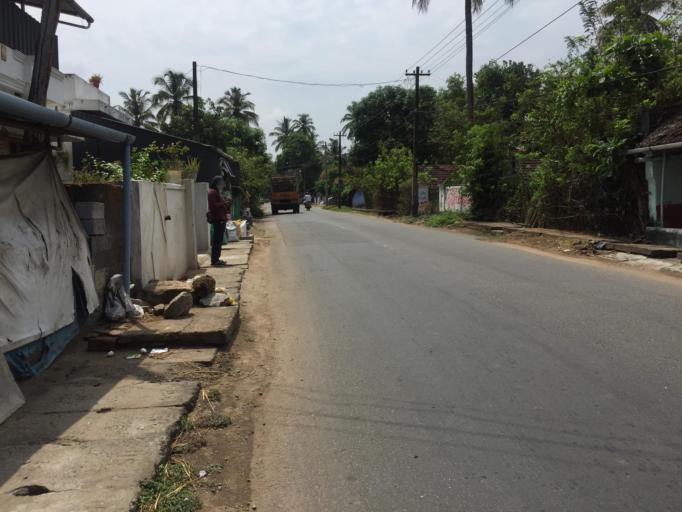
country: IN
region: Kerala
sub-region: Palakkad district
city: Chittur
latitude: 10.6816
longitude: 76.7139
